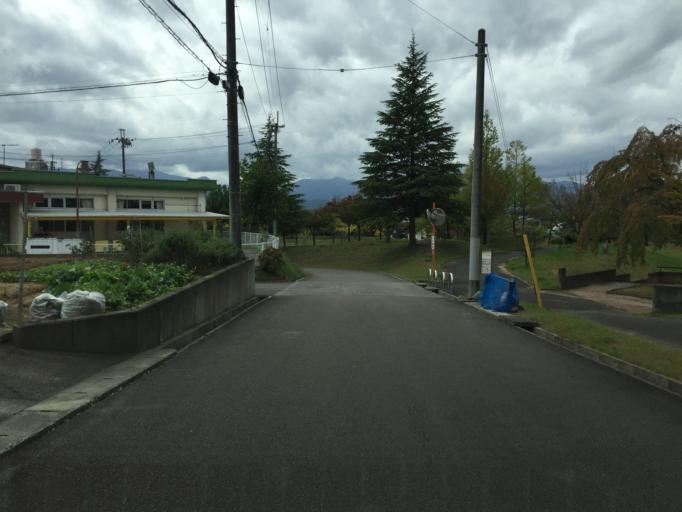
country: JP
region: Fukushima
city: Fukushima-shi
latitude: 37.6975
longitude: 140.4754
